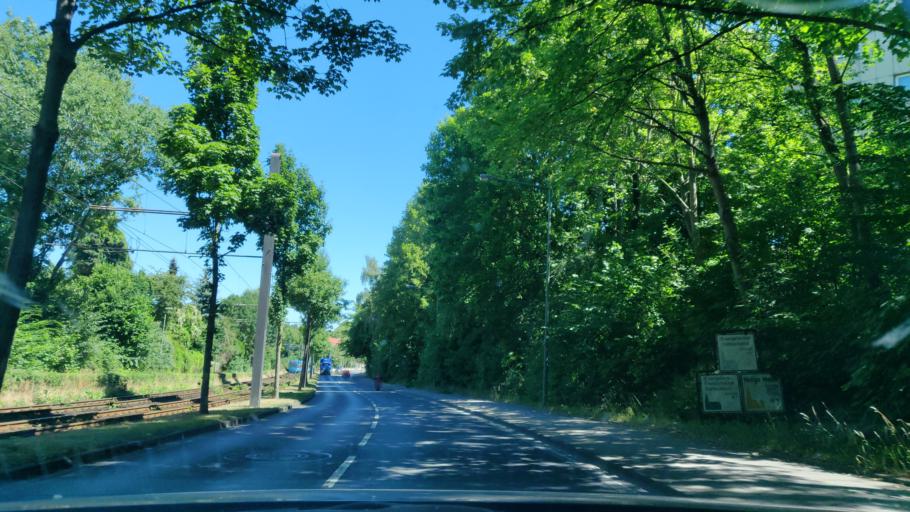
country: DE
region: Hesse
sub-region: Regierungsbezirk Kassel
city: Baunatal
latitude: 51.2701
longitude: 9.4396
